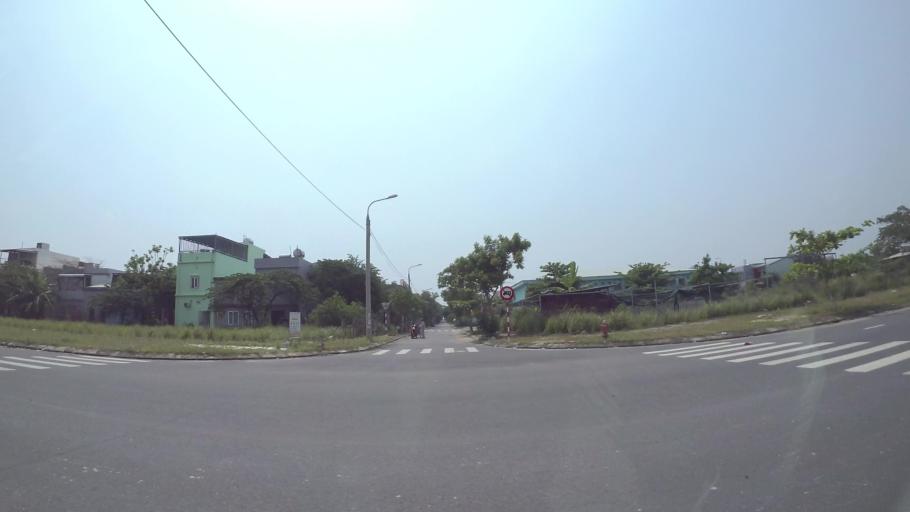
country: VN
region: Da Nang
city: Cam Le
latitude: 15.9945
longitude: 108.2117
